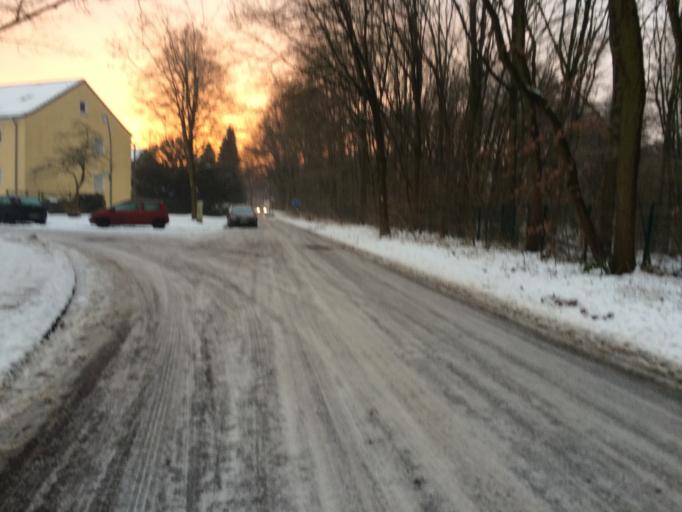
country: DE
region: North Rhine-Westphalia
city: Dorsten
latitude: 51.6696
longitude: 7.0012
